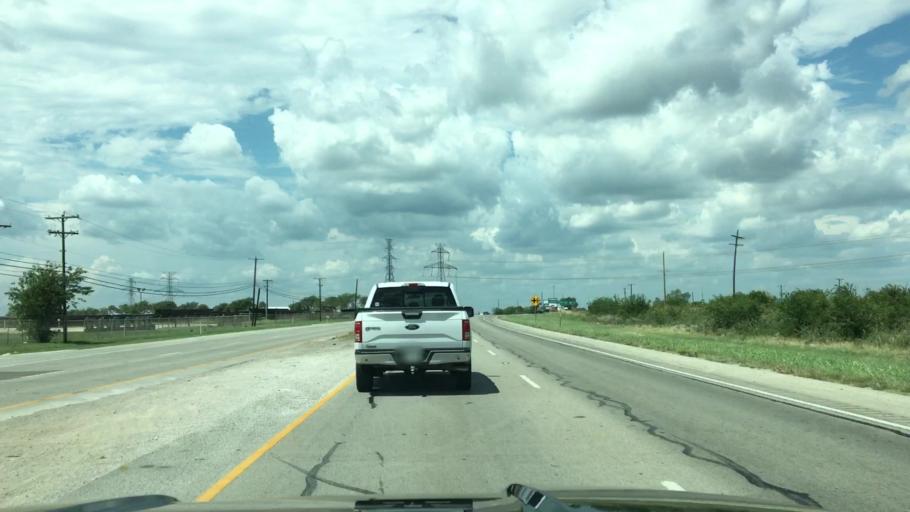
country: US
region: Texas
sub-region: Tarrant County
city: Eagle Mountain
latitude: 32.9026
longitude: -97.4006
